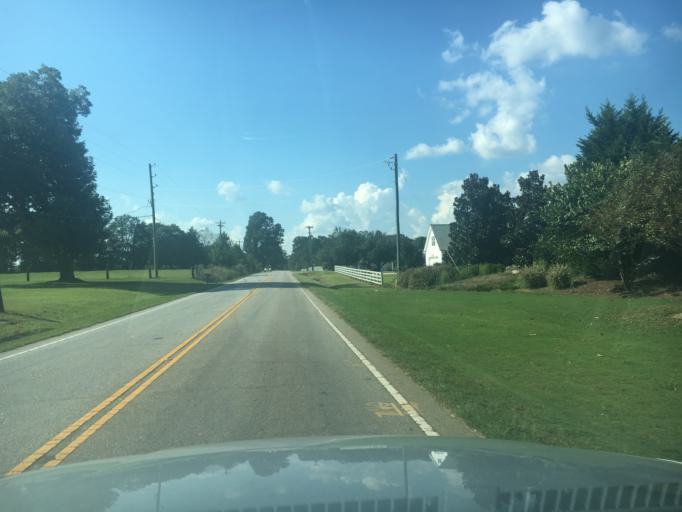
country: US
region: South Carolina
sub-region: Greenville County
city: Fountain Inn
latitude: 34.6256
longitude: -82.2445
